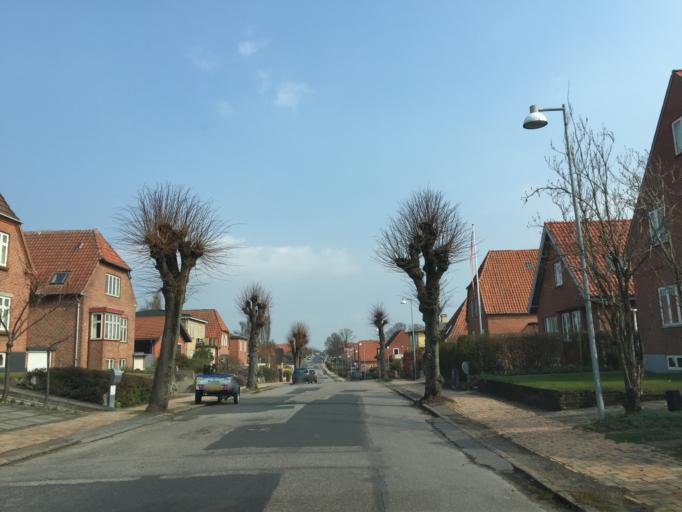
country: DK
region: South Denmark
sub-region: Odense Kommune
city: Odense
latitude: 55.4093
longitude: 10.4019
